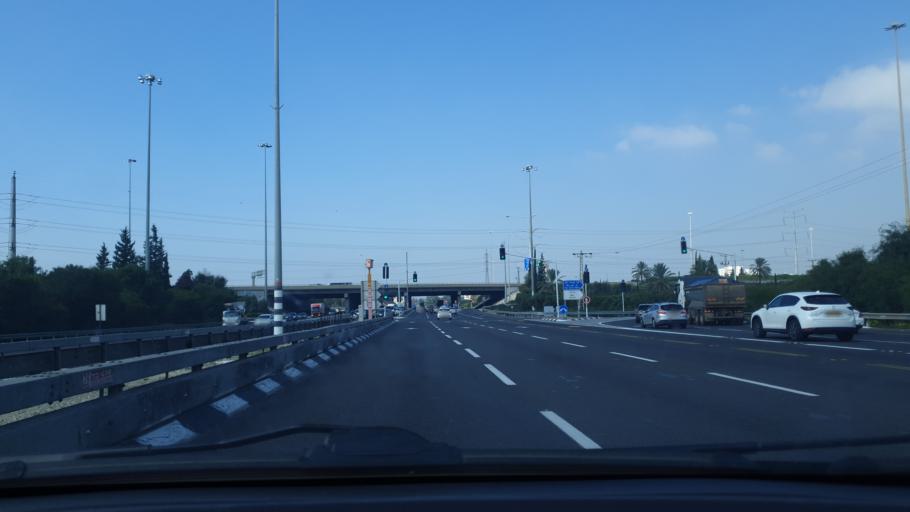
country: IL
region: Central District
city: Bet Dagan
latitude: 32.0084
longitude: 34.8158
